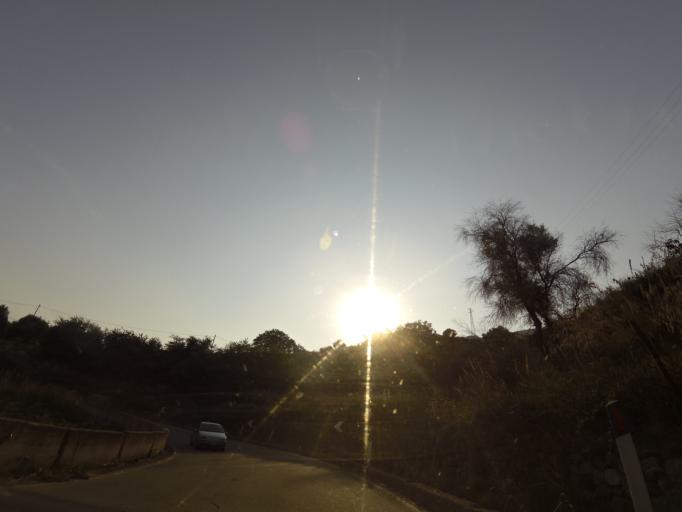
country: IT
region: Calabria
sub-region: Provincia di Reggio Calabria
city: Stilo
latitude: 38.4732
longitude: 16.4725
